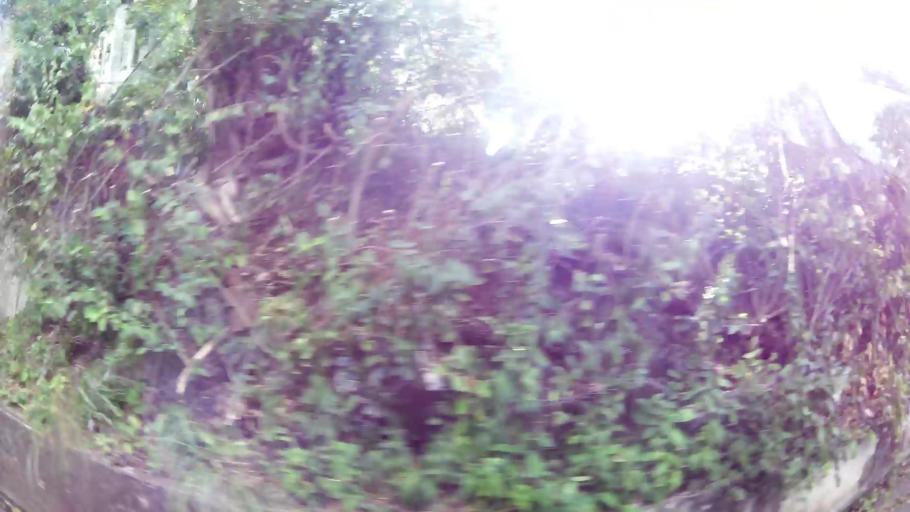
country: MQ
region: Martinique
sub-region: Martinique
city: Fort-de-France
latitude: 14.6398
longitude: -61.1353
